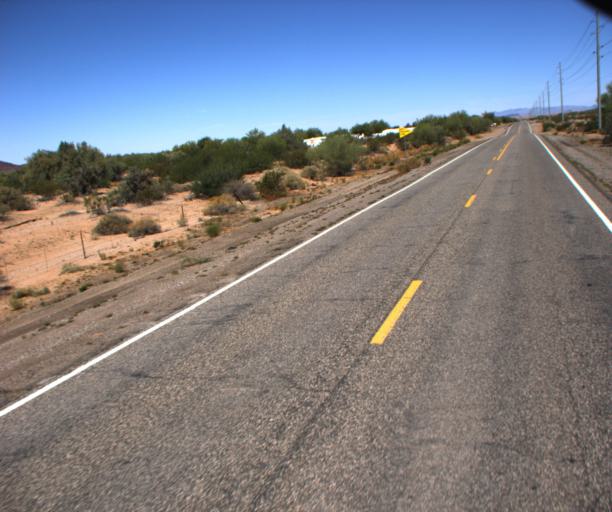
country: US
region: Arizona
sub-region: La Paz County
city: Cienega Springs
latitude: 33.9490
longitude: -114.0194
